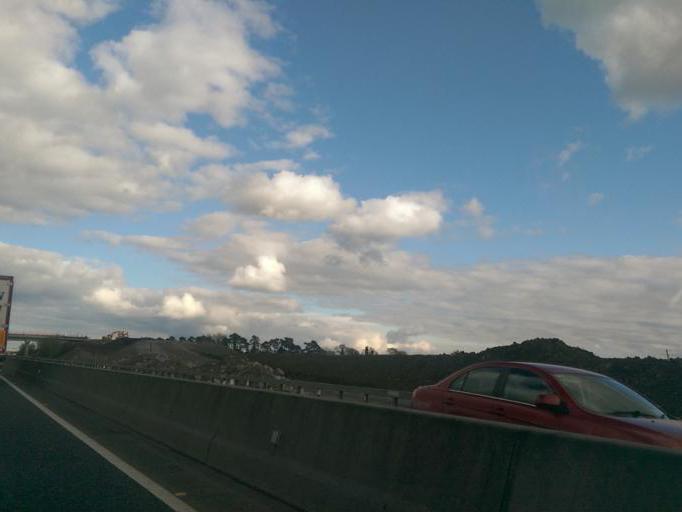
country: IE
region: Leinster
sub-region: An Iarmhi
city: Moate
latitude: 53.4001
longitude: -7.8342
